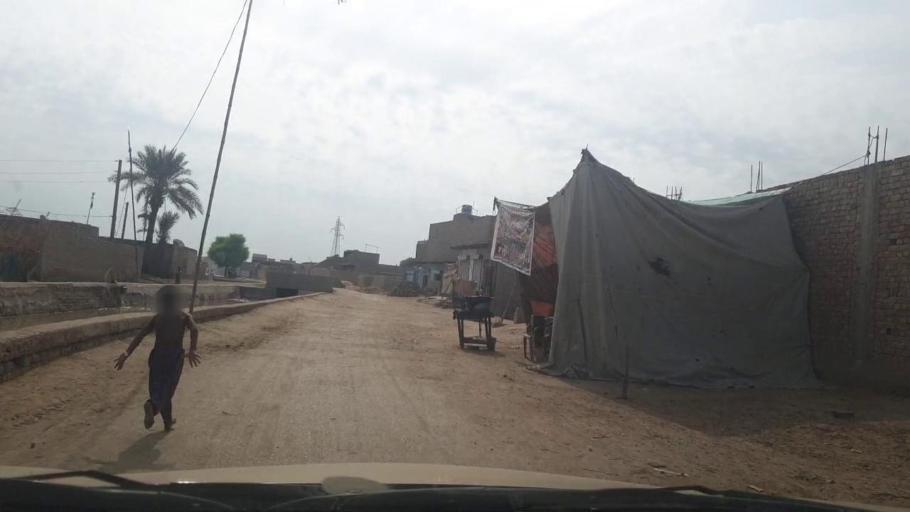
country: PK
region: Sindh
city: Larkana
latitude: 27.5814
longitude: 68.2047
